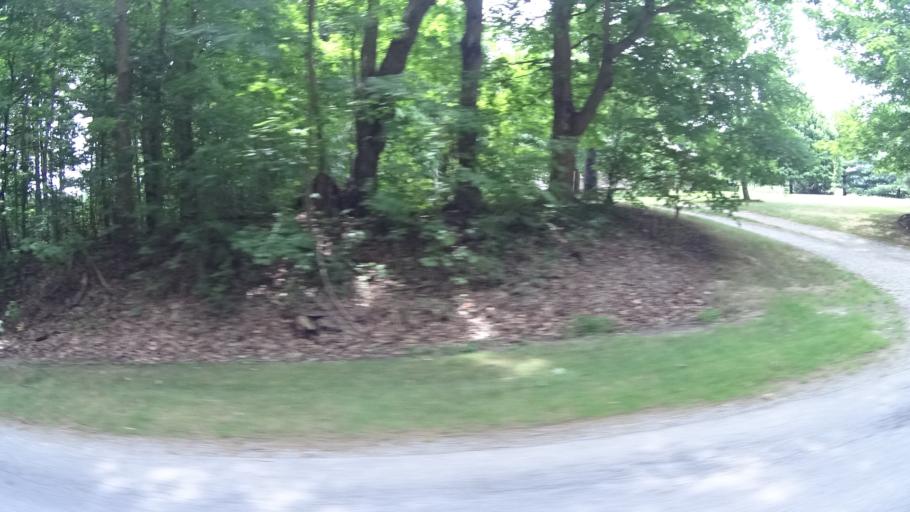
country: US
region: Ohio
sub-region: Erie County
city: Milan
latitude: 41.2874
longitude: -82.6563
